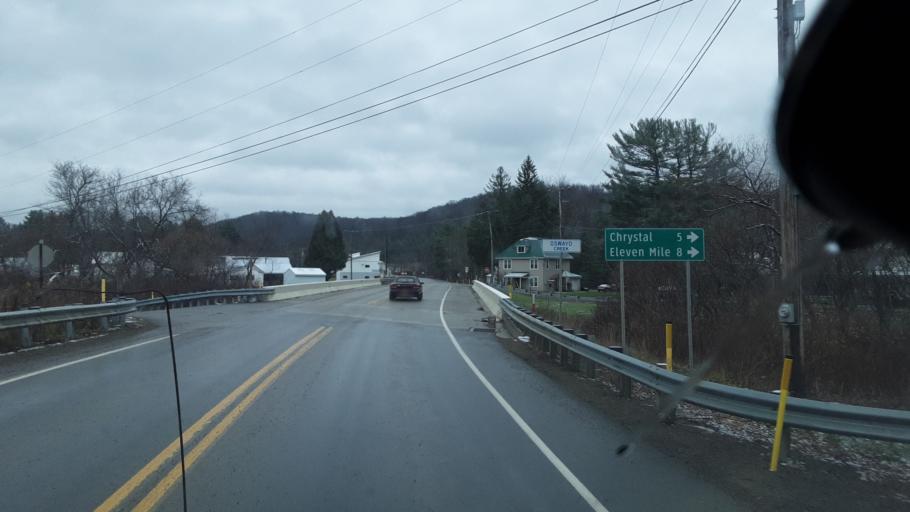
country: US
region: Pennsylvania
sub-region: Potter County
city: Shinglehouse
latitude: 41.9236
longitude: -78.1194
